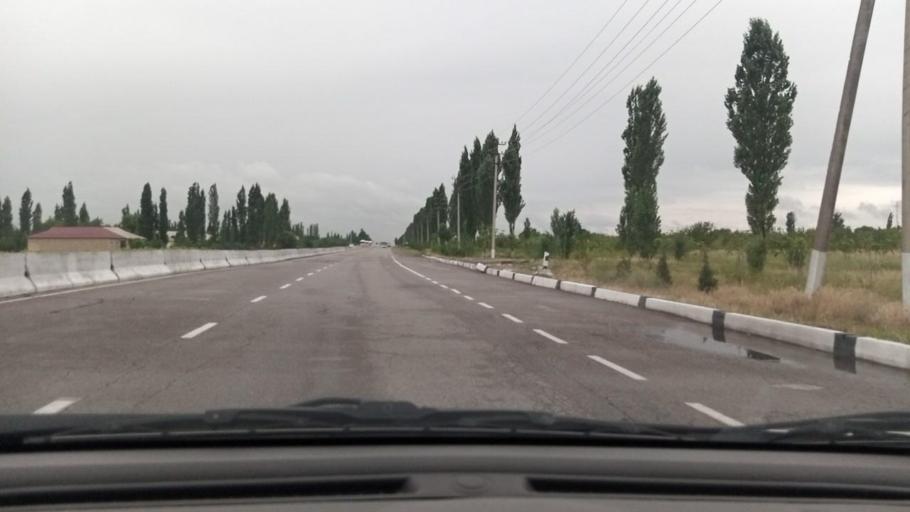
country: UZ
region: Toshkent
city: Ohangaron
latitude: 40.9155
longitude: 69.8282
